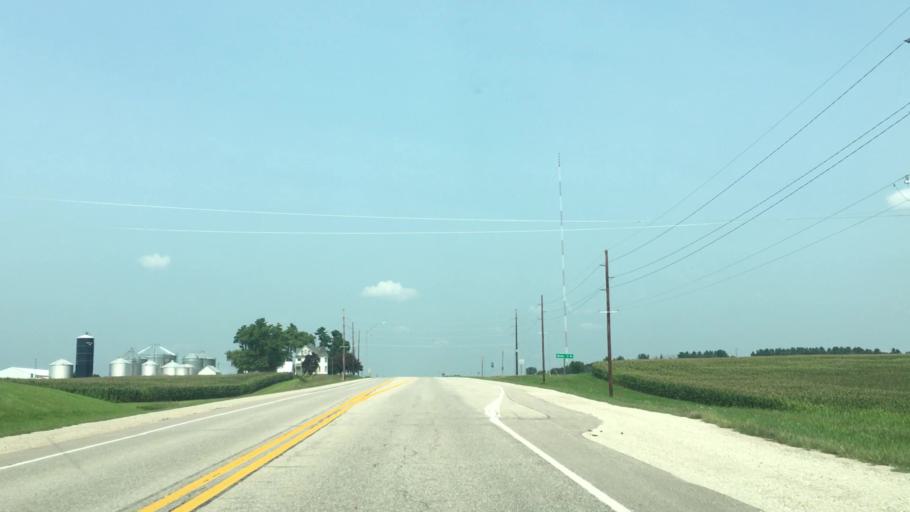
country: US
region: Iowa
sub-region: Benton County
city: Urbana
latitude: 42.2810
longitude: -91.8901
